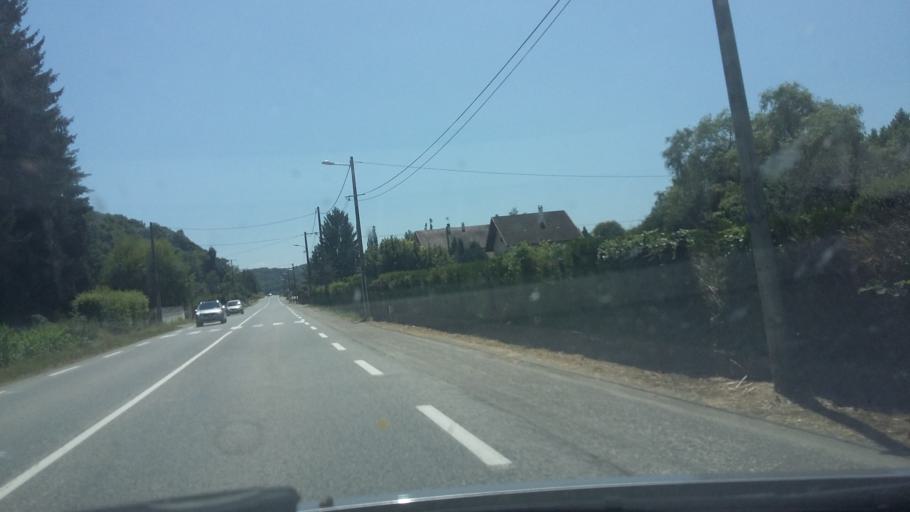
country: FR
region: Rhone-Alpes
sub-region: Departement de l'Ain
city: Belley
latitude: 45.7996
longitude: 5.6821
